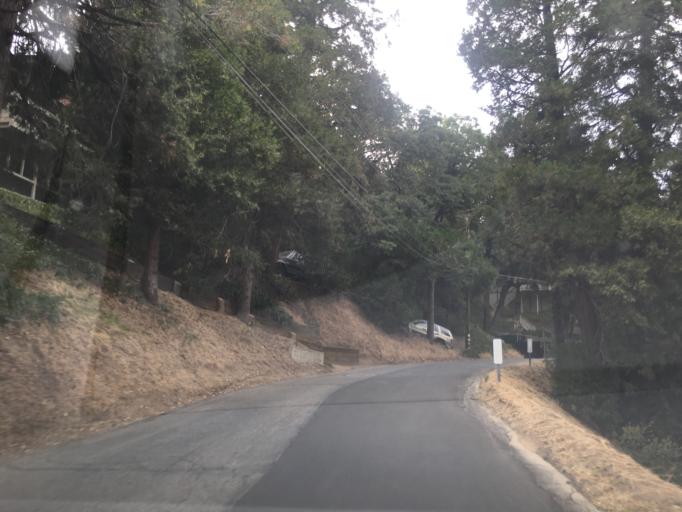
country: US
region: California
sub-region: San Bernardino County
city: Crestline
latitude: 34.2465
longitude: -117.2739
